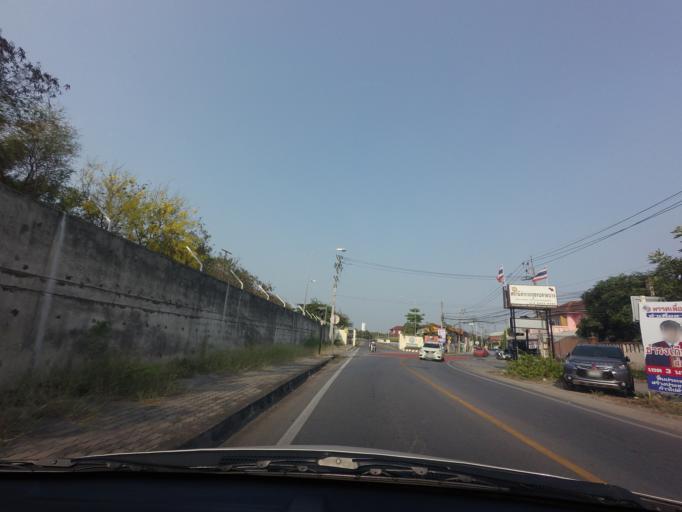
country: TH
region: Nonthaburi
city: Bang Yai
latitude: 13.8046
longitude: 100.4021
